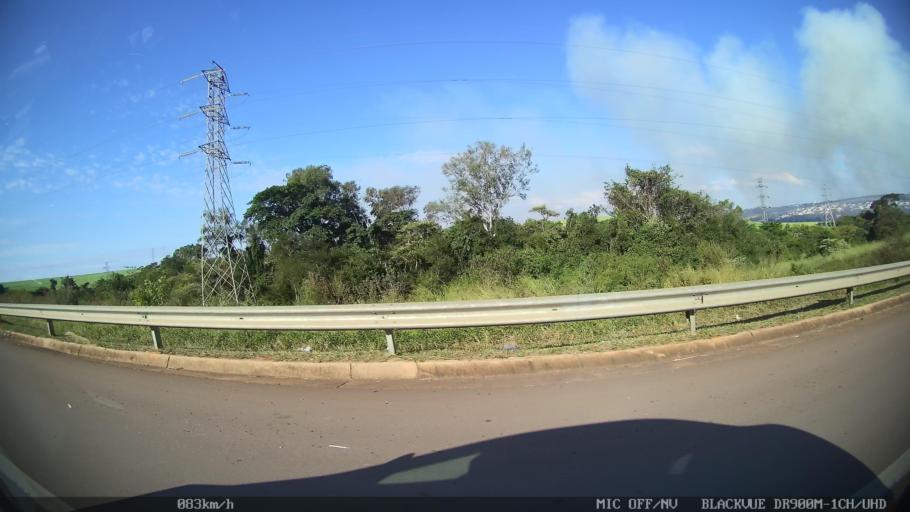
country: BR
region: Sao Paulo
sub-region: Piracicaba
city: Piracicaba
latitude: -22.6886
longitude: -47.5983
